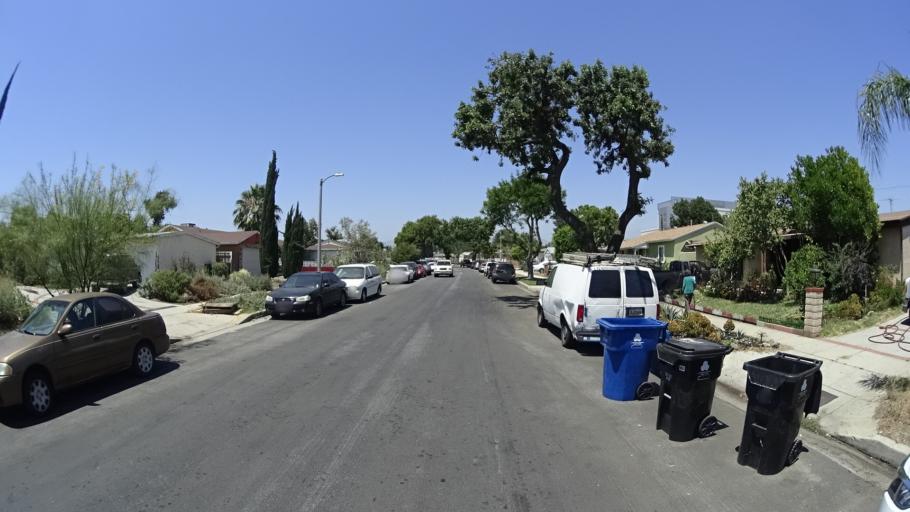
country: US
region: California
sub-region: Los Angeles County
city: Van Nuys
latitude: 34.2166
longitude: -118.4320
